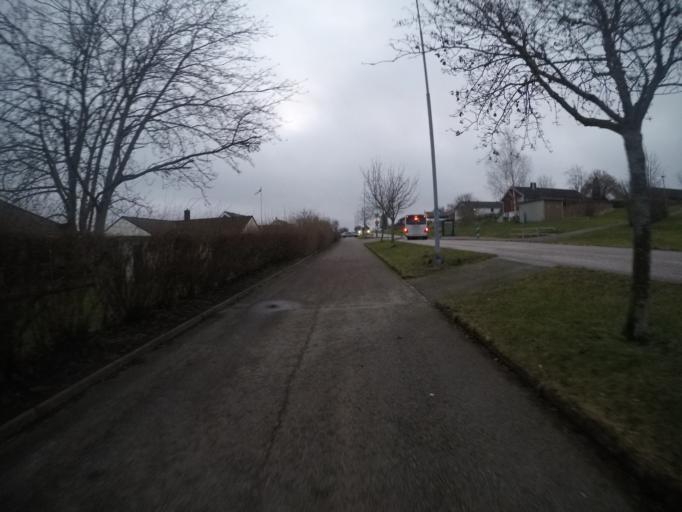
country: SE
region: Halland
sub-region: Laholms Kommun
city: Laholm
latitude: 56.5056
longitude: 13.0218
